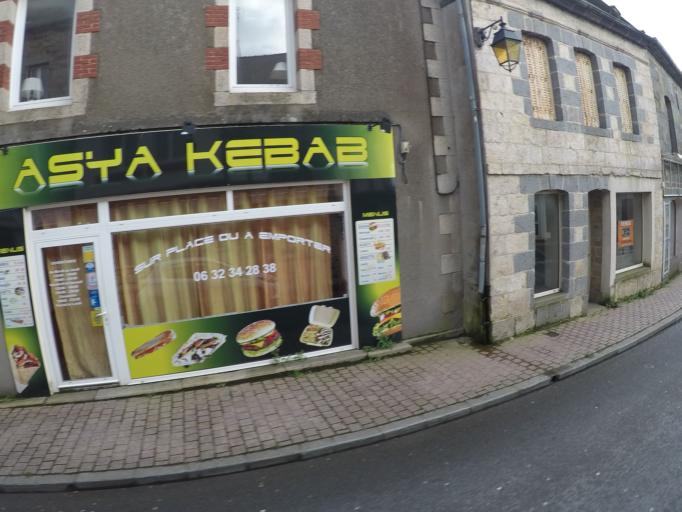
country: FR
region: Brittany
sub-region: Departement des Cotes-d'Armor
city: Lanvollon
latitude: 48.6309
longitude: -2.9860
